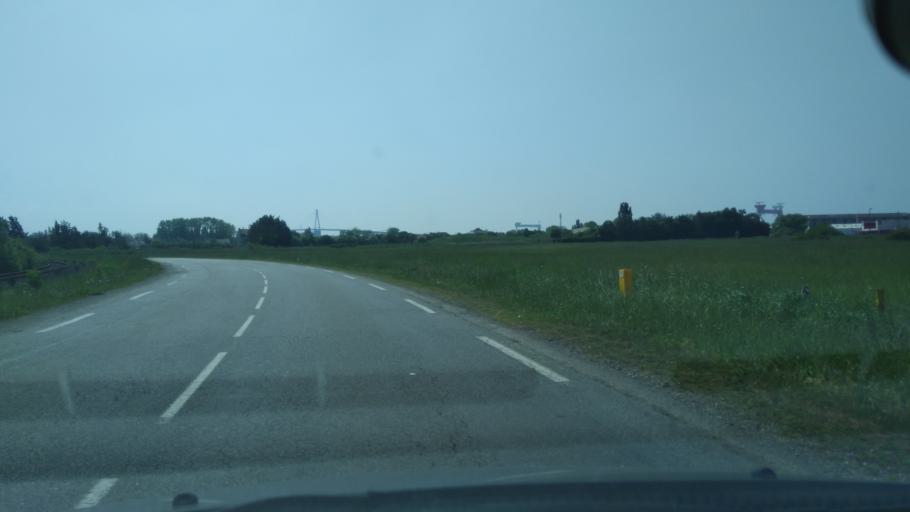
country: FR
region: Pays de la Loire
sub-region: Departement de la Loire-Atlantique
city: Trignac
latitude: 47.3079
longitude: -2.1729
